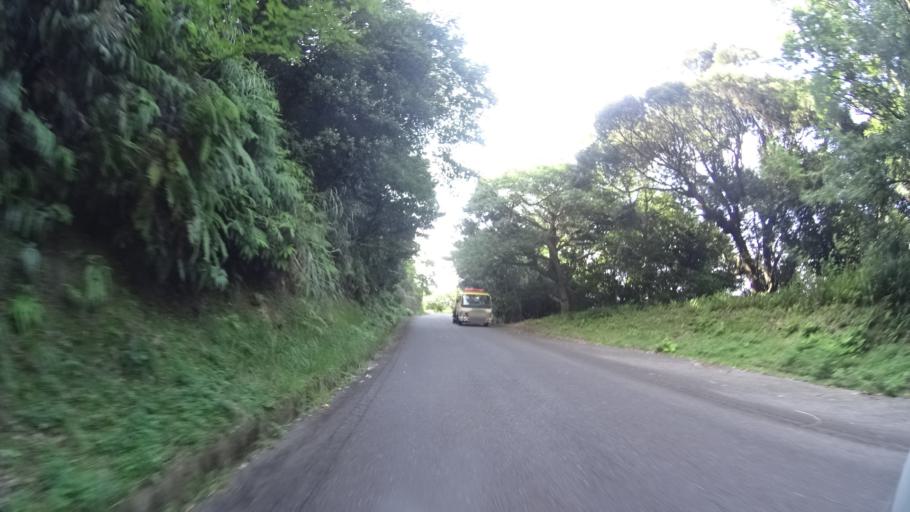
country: JP
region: Kagoshima
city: Nishinoomote
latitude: 30.3894
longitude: 130.3902
